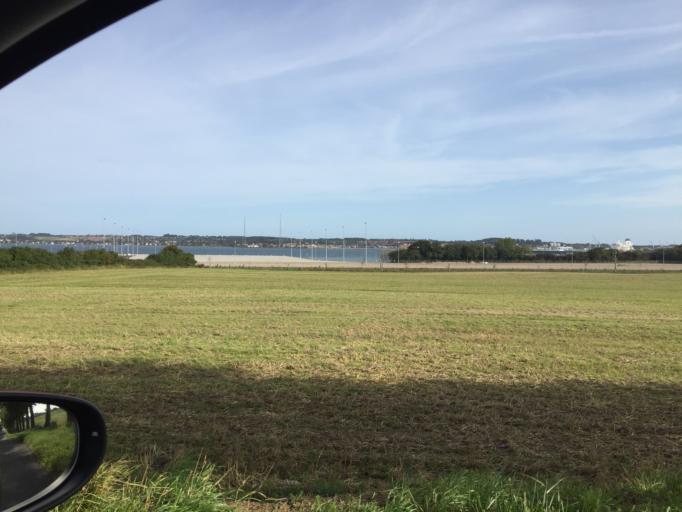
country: DK
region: Zealand
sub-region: Kalundborg Kommune
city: Kalundborg
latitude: 55.6574
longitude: 11.0645
